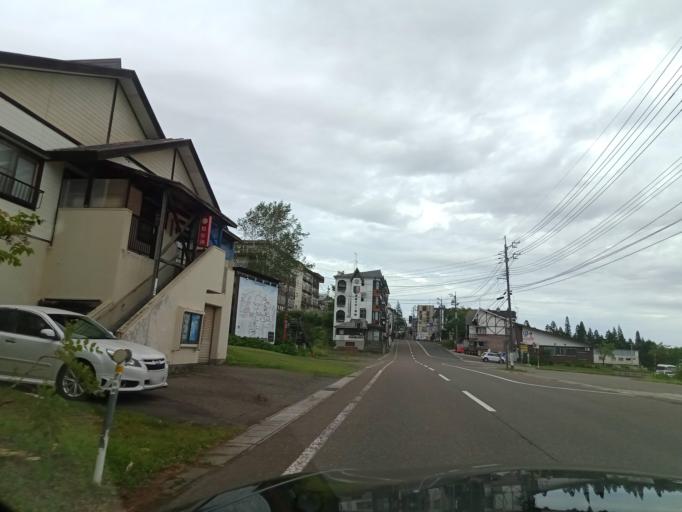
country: JP
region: Niigata
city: Arai
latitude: 36.8904
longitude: 138.1770
